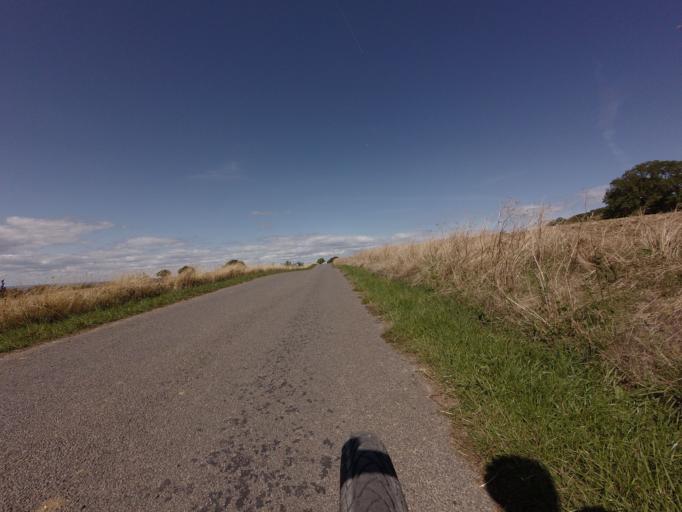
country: DK
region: Zealand
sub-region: Vordingborg Kommune
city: Stege
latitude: 55.0167
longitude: 12.4591
